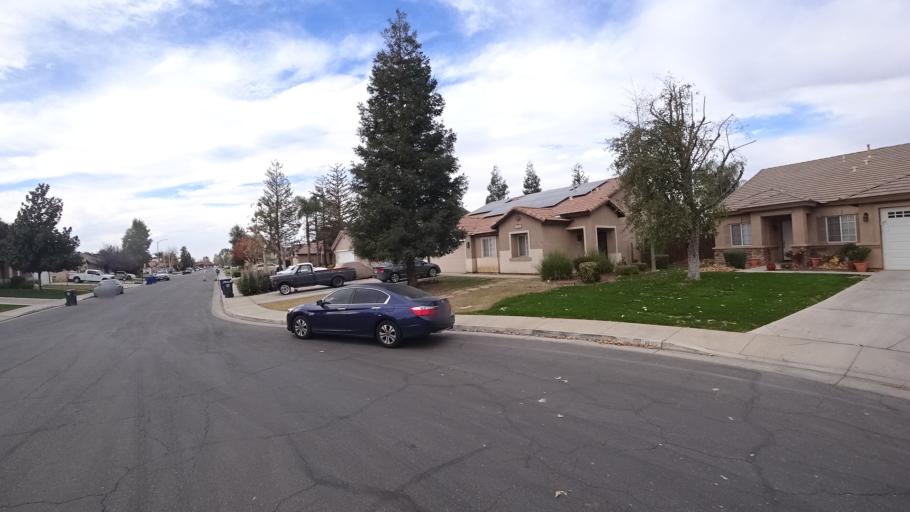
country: US
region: California
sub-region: Kern County
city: Rosedale
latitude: 35.4174
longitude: -119.1327
